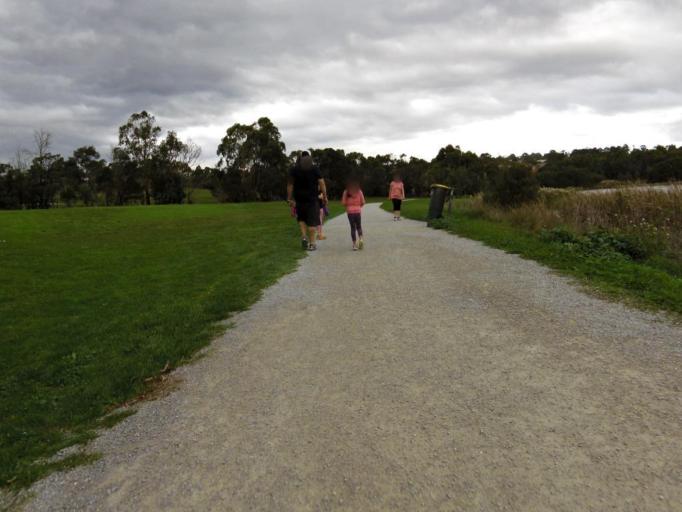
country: AU
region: Victoria
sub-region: Yarra Ranges
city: Lilydale
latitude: -37.7679
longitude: 145.3545
